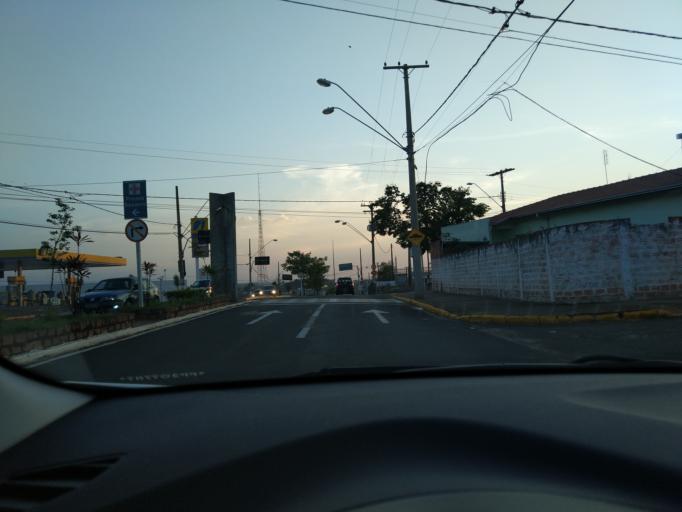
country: BR
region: Sao Paulo
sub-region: Botucatu
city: Botucatu
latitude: -22.8991
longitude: -48.4486
